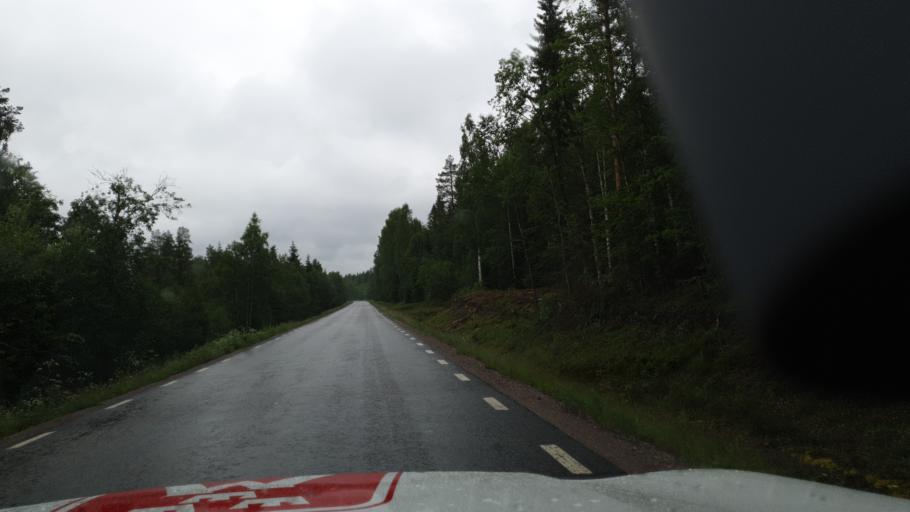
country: SE
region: Vaesterbotten
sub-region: Vannas Kommun
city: Vannasby
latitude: 63.8245
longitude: 19.8566
